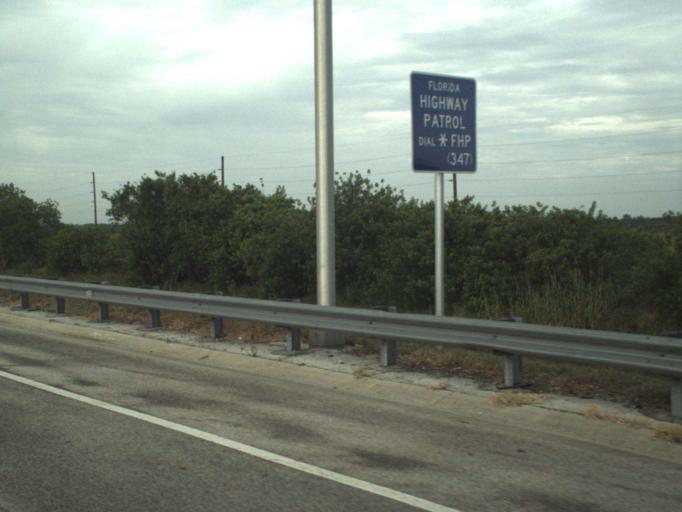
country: US
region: Florida
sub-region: Saint Lucie County
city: Port Saint Lucie
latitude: 27.2045
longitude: -80.4008
